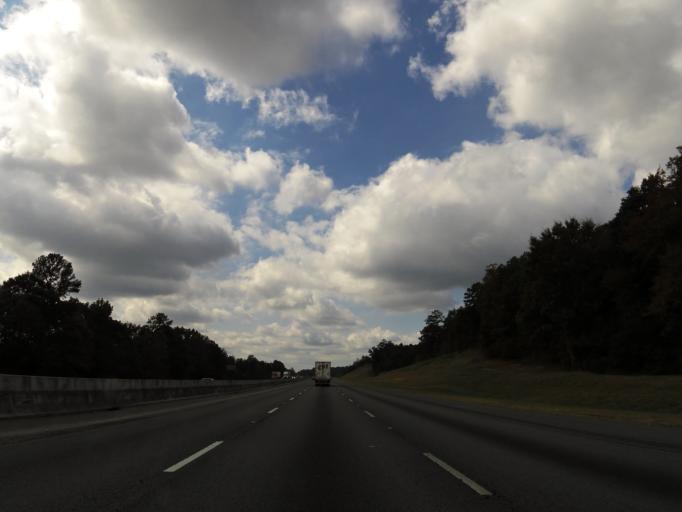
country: US
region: Alabama
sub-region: Tuscaloosa County
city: Lake View
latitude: 33.3105
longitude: -87.0613
